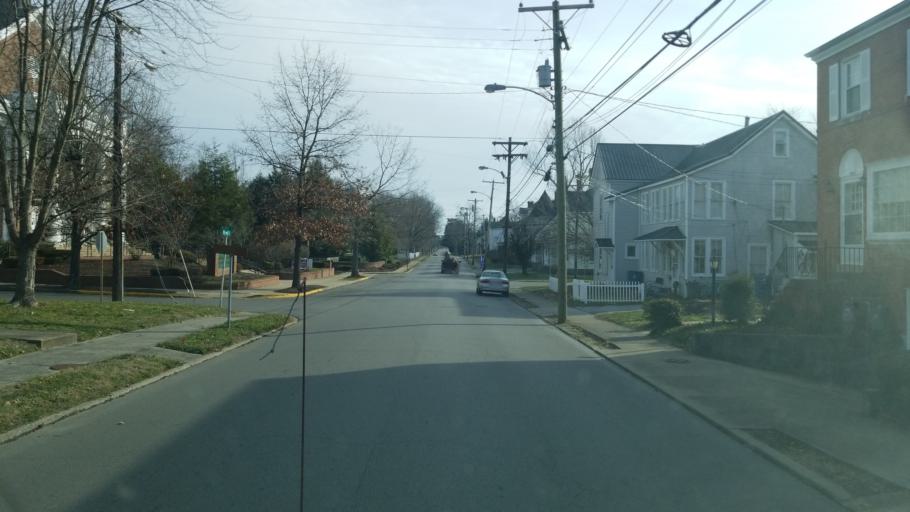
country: US
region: Kentucky
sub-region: Boyle County
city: Danville
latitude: 37.6491
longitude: -84.7745
